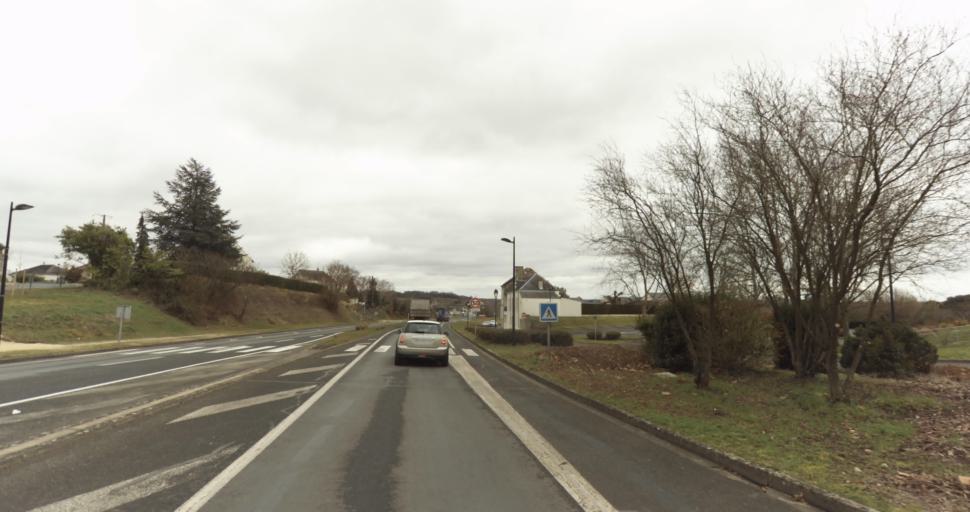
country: FR
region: Pays de la Loire
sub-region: Departement de Maine-et-Loire
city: Varrains
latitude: 47.2266
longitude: -0.0672
